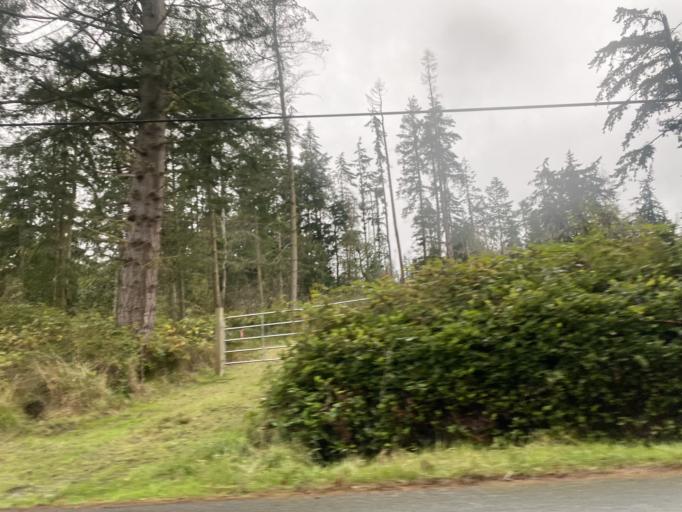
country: US
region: Washington
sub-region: Island County
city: Freeland
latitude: 48.0868
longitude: -122.4849
